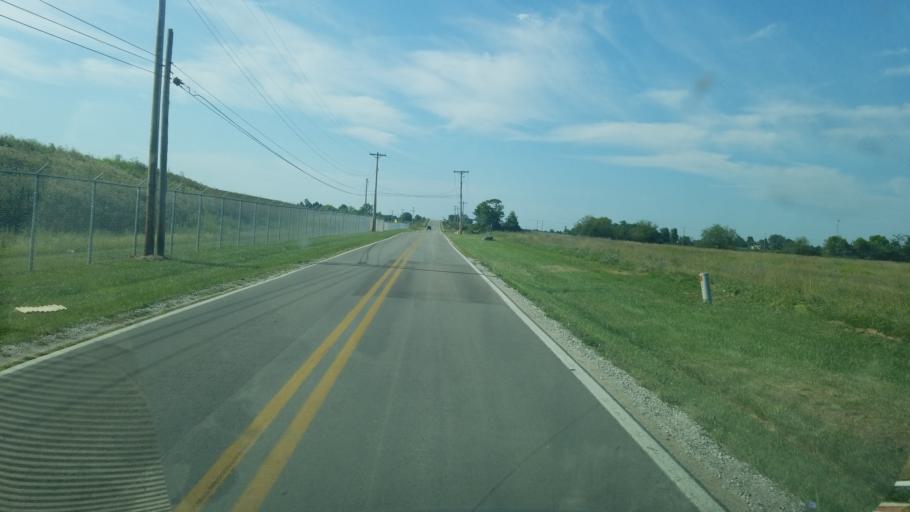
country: US
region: Ohio
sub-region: Franklin County
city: Grove City
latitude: 39.8338
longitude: -83.1186
